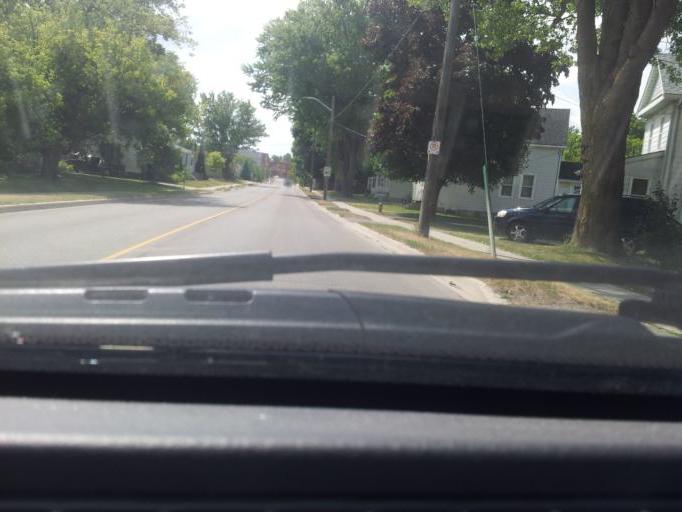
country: CA
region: Ontario
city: Stratford
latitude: 43.3631
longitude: -80.9843
